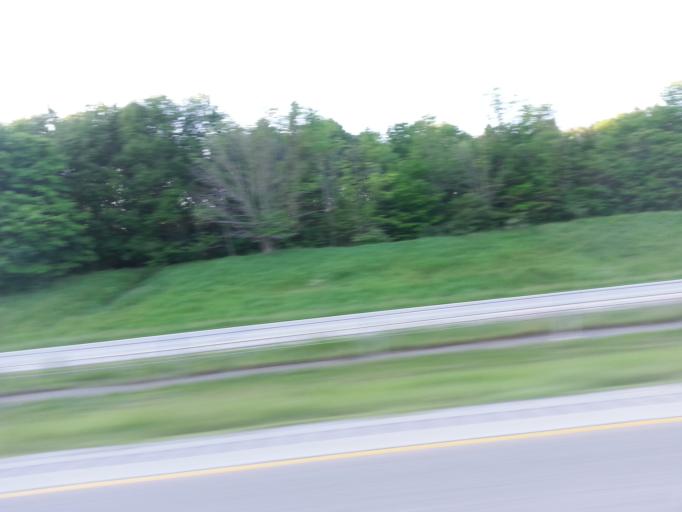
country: US
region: Illinois
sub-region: Vermilion County
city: Danville
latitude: 40.1148
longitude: -87.5760
